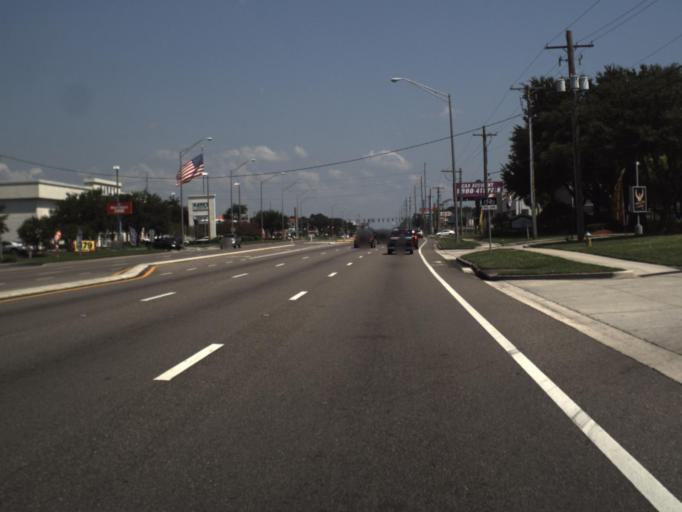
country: US
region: Florida
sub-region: Hillsborough County
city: Egypt Lake-Leto
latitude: 28.0037
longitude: -82.5051
